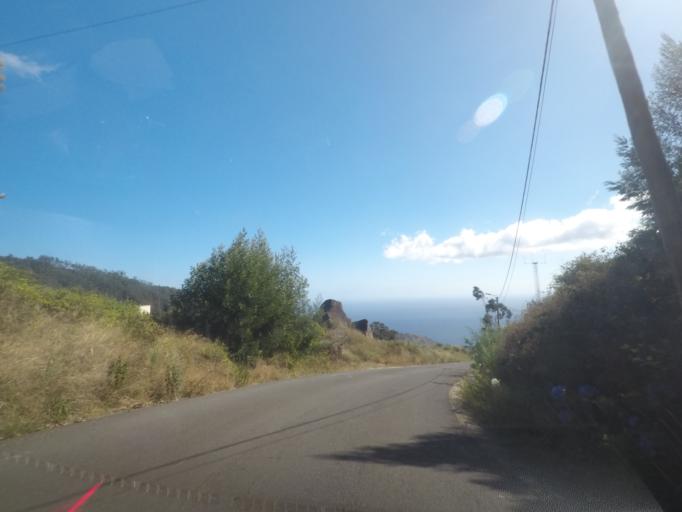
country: PT
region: Madeira
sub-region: Ribeira Brava
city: Campanario
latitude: 32.6829
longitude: -17.0235
